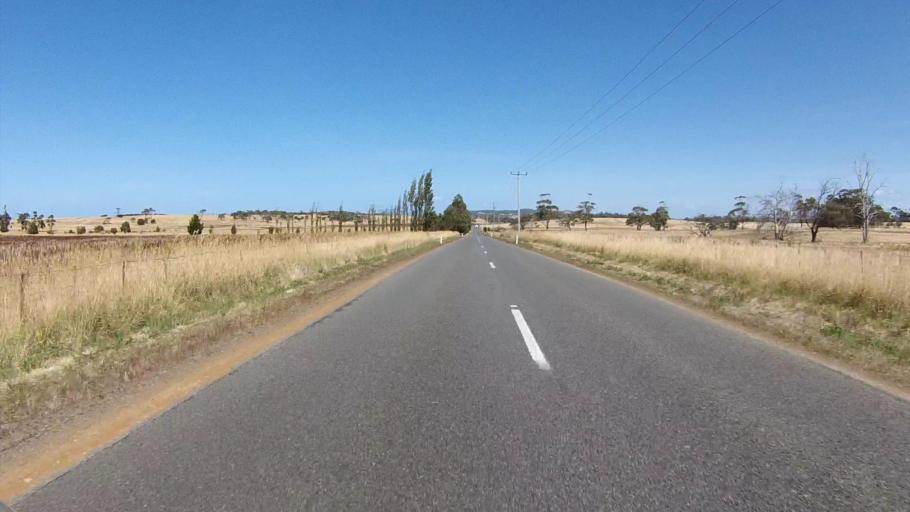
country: AU
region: Tasmania
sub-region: Sorell
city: Sorell
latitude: -42.2696
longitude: 148.0037
